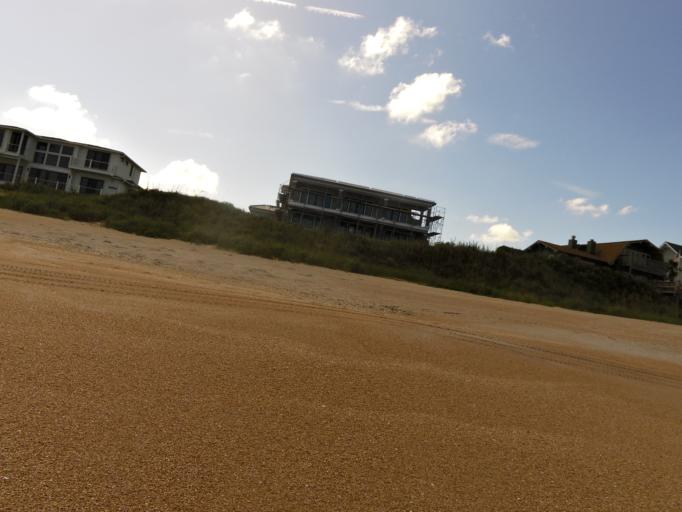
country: US
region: Florida
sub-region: Saint Johns County
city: Palm Valley
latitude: 30.0629
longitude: -81.3318
